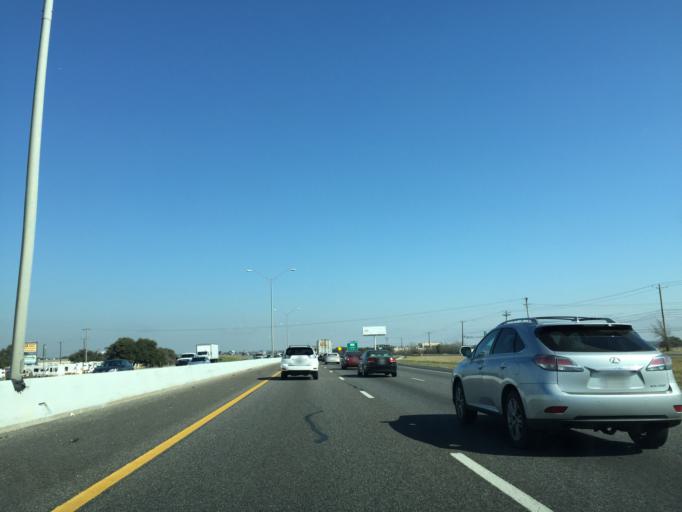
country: US
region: Texas
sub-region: Williamson County
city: Georgetown
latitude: 30.6006
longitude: -97.6881
